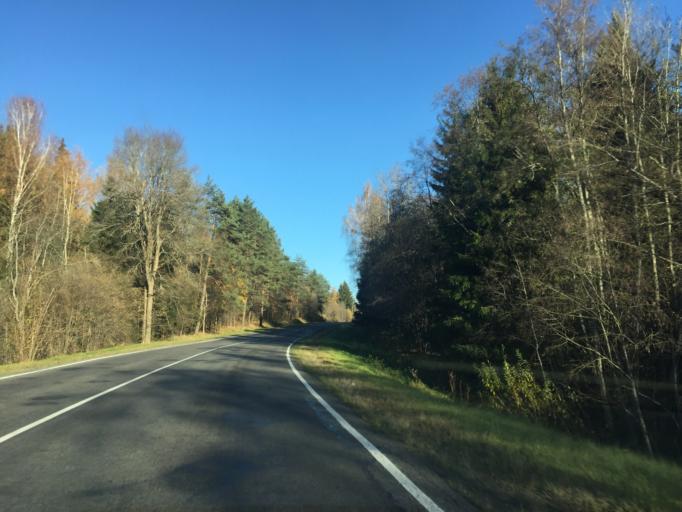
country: BY
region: Vitebsk
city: Dzisna
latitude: 55.3687
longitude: 28.3693
